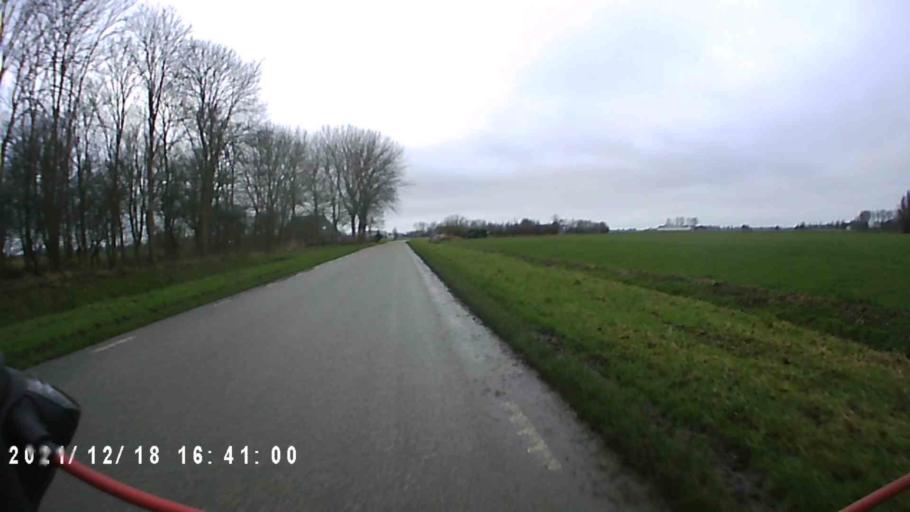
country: NL
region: Friesland
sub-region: Gemeente Dongeradeel
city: Ternaard
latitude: 53.3622
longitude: 5.9999
